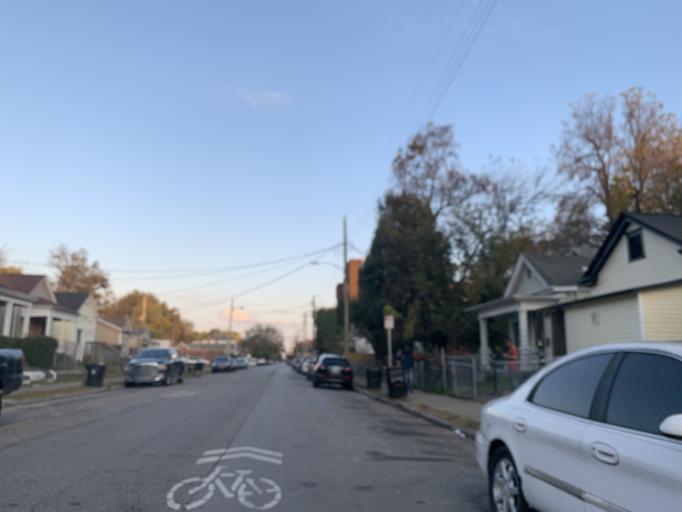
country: US
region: Kentucky
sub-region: Jefferson County
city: Louisville
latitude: 38.2543
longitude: -85.7957
